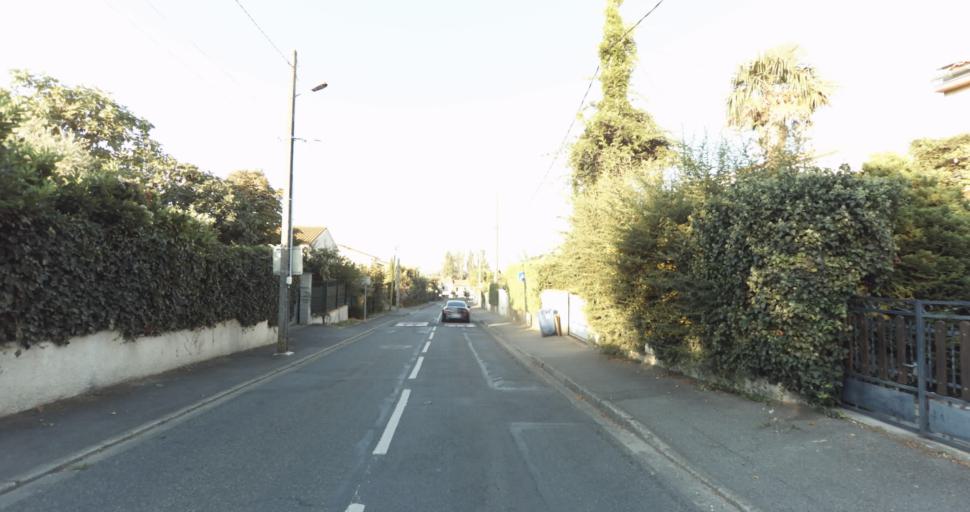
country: FR
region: Midi-Pyrenees
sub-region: Departement de la Haute-Garonne
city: L'Union
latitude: 43.6600
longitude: 1.4810
